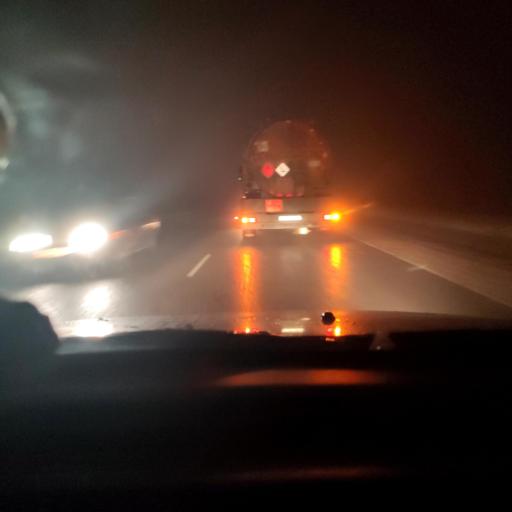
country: RU
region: Samara
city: Dubovyy Umet
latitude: 52.9563
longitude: 50.3014
